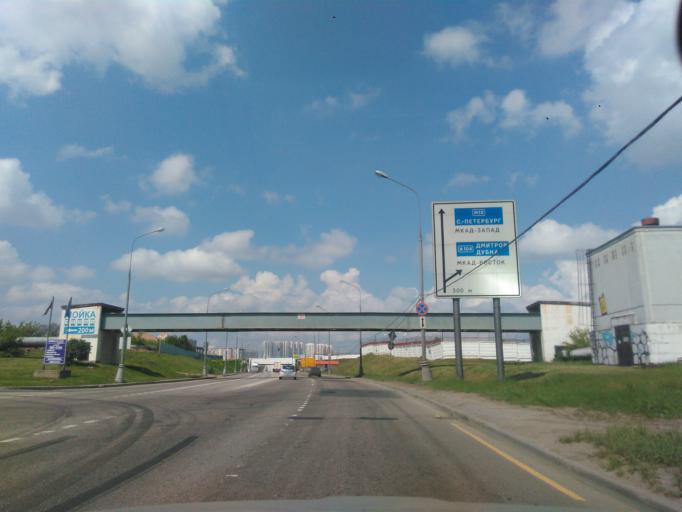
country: RU
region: Moscow
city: Businovo
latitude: 55.8889
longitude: 37.5023
